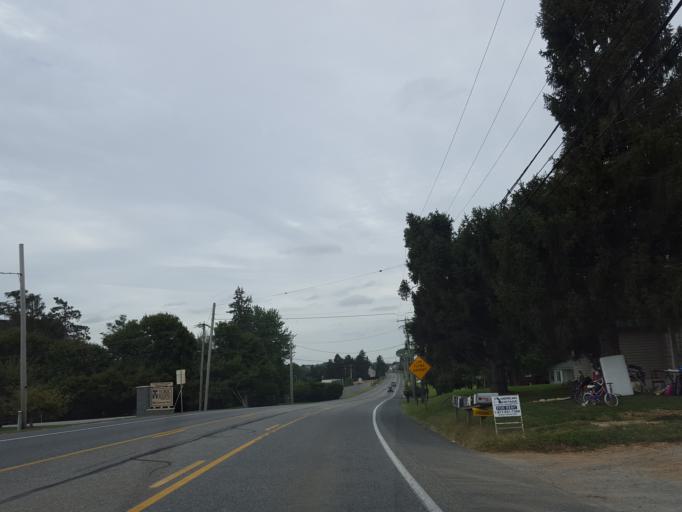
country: US
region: Pennsylvania
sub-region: York County
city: Spring Grove
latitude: 39.9240
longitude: -76.8740
